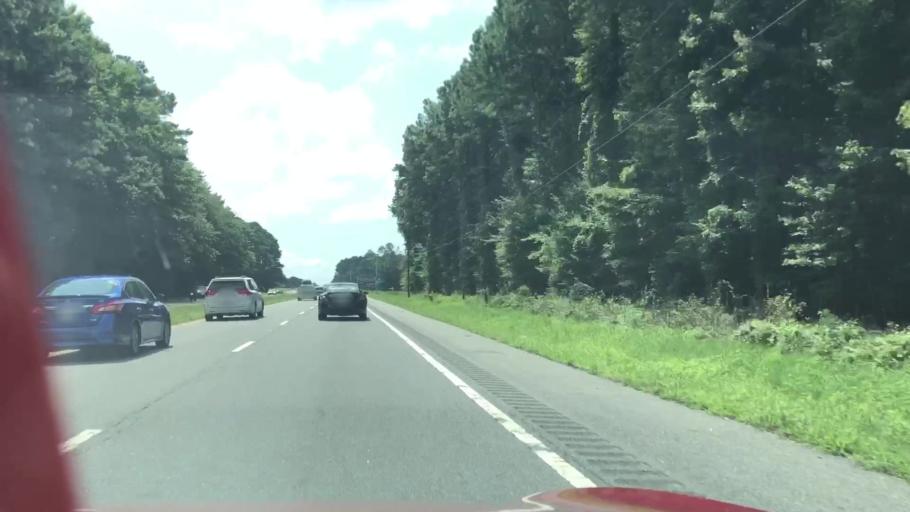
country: US
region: Virginia
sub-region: Northampton County
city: Cape Charles
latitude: 37.2582
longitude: -75.9737
